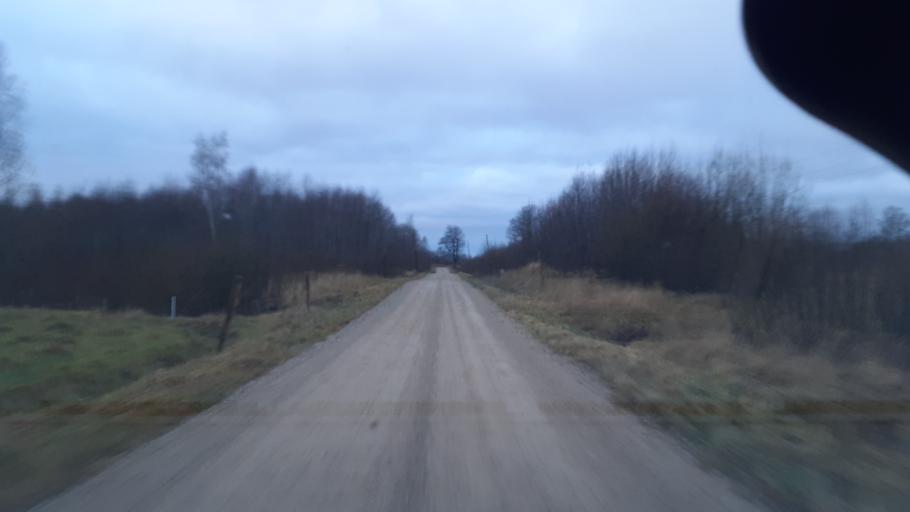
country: LV
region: Alsunga
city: Alsunga
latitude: 56.9047
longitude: 21.6879
